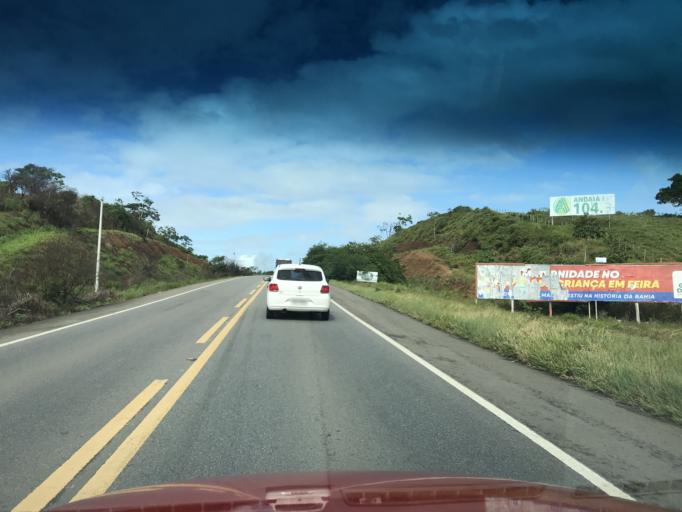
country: BR
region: Bahia
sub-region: Conceicao Do Almeida
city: Muritiba
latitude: -12.9109
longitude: -39.2410
